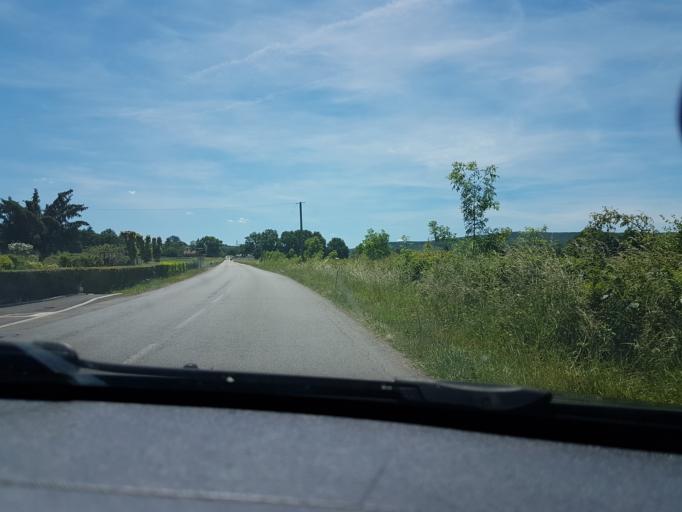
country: FR
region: Bourgogne
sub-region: Departement de Saone-et-Loire
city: Epinac
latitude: 46.9825
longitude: 4.5079
